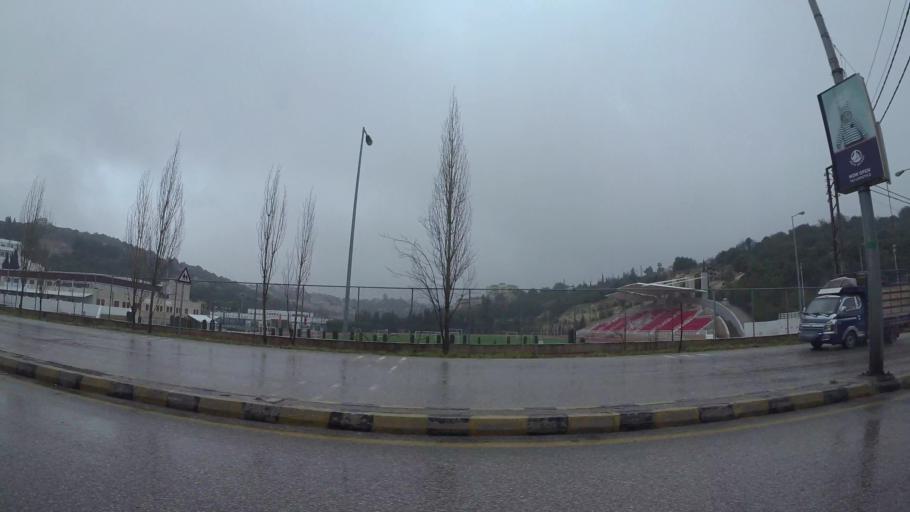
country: JO
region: Amman
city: Wadi as Sir
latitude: 32.0016
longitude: 35.8025
